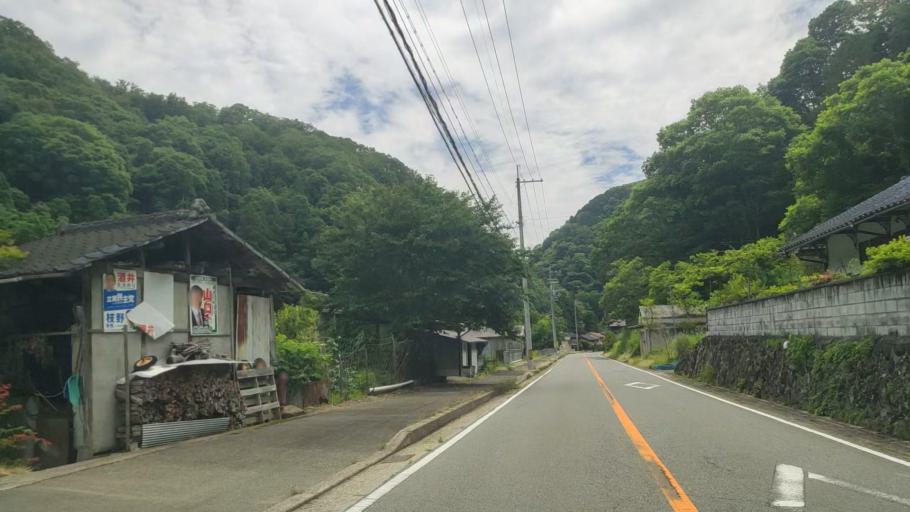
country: JP
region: Hyogo
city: Yamazakicho-nakabirose
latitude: 35.0980
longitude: 134.3628
